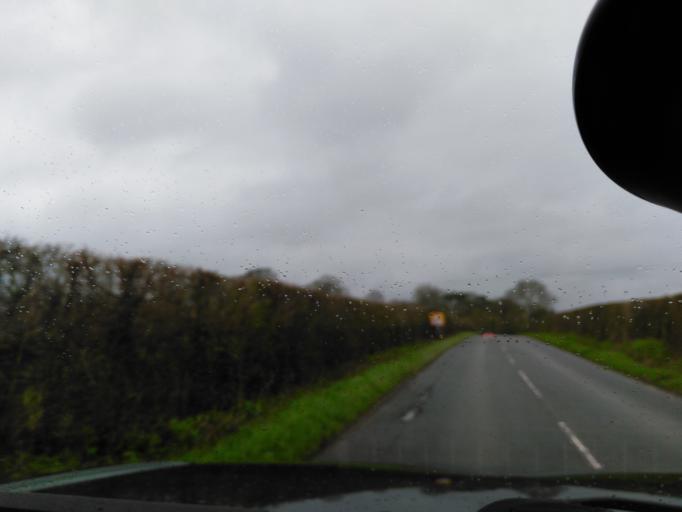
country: GB
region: England
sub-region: Wiltshire
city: Wingfield
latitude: 51.3230
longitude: -2.2579
